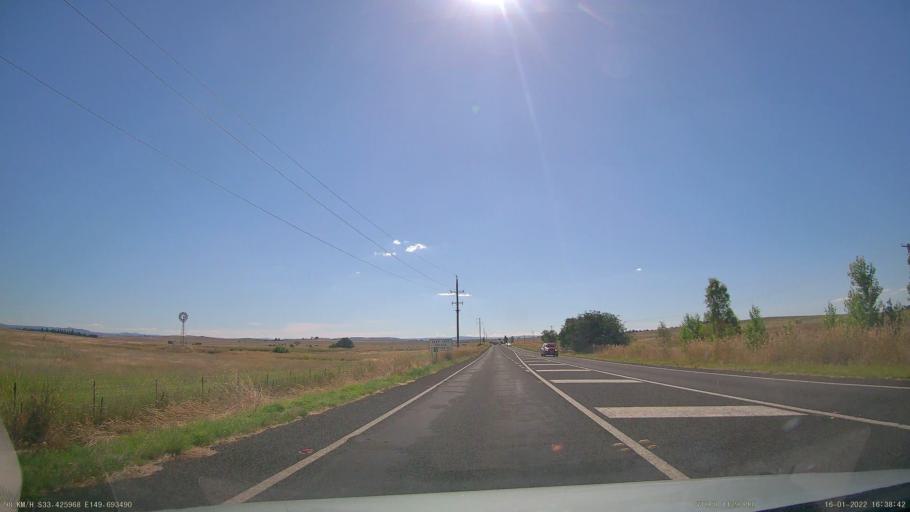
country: AU
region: New South Wales
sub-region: Bathurst Regional
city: Kelso
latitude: -33.4257
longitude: 149.6929
